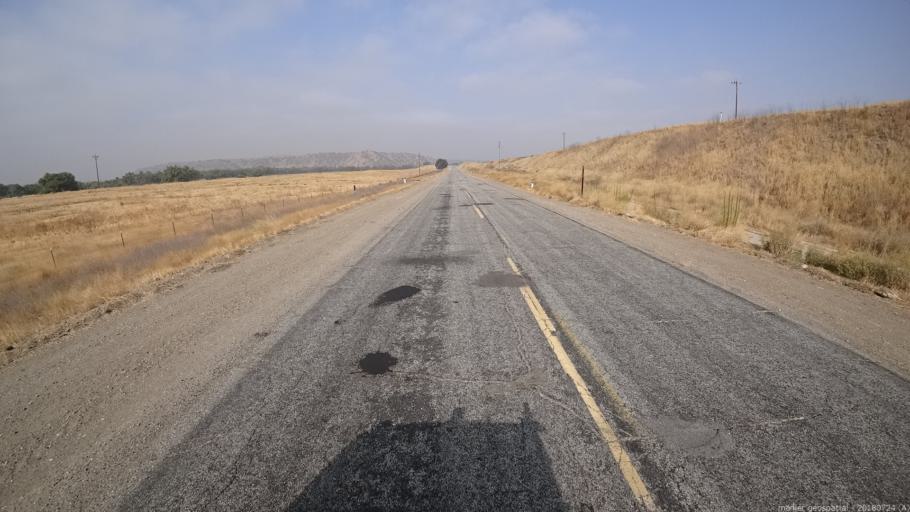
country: US
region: California
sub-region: San Luis Obispo County
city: San Miguel
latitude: 35.8621
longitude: -120.7837
